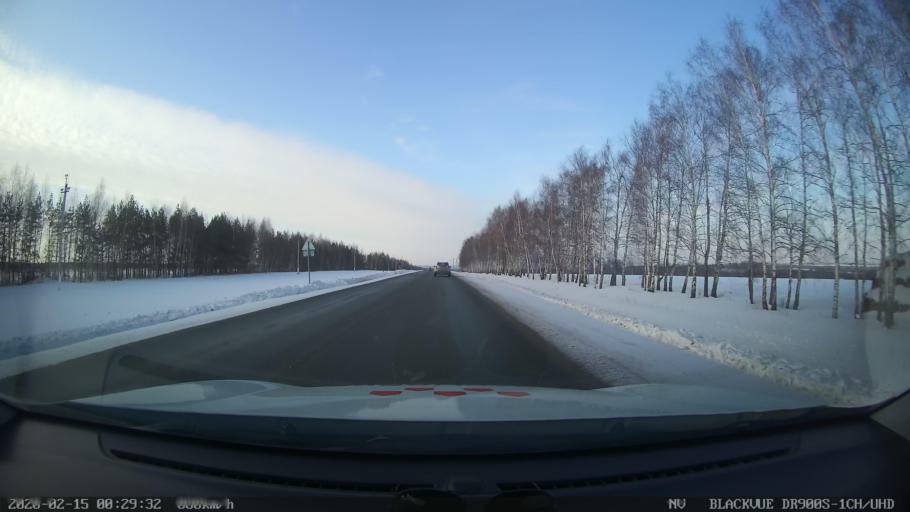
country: RU
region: Tatarstan
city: Verkhniy Uslon
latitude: 55.6516
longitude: 48.8673
